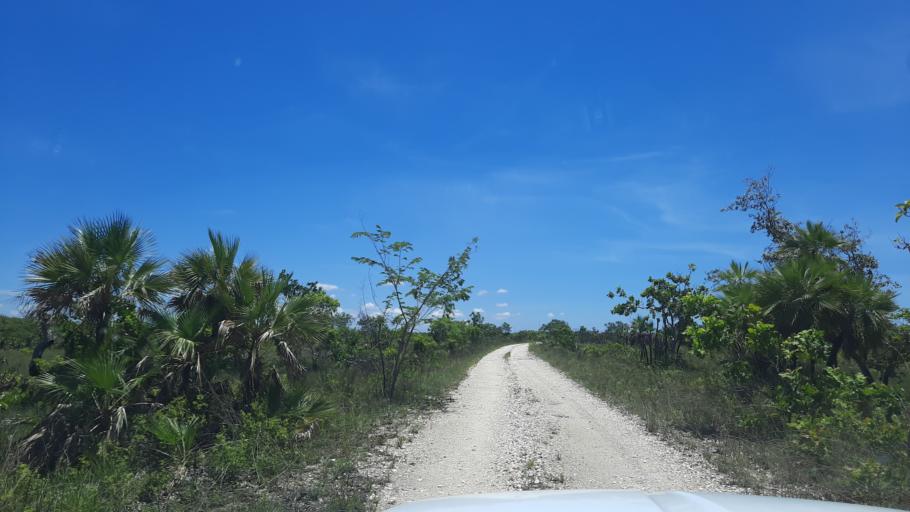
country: BZ
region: Cayo
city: Belmopan
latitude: 17.3838
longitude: -88.4956
